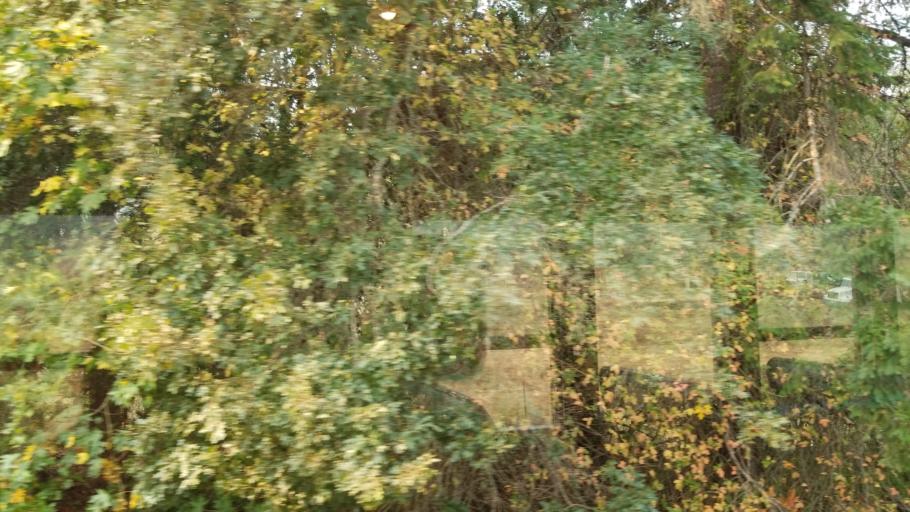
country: US
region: California
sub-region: Mendocino County
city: Willits
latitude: 39.4064
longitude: -123.3776
